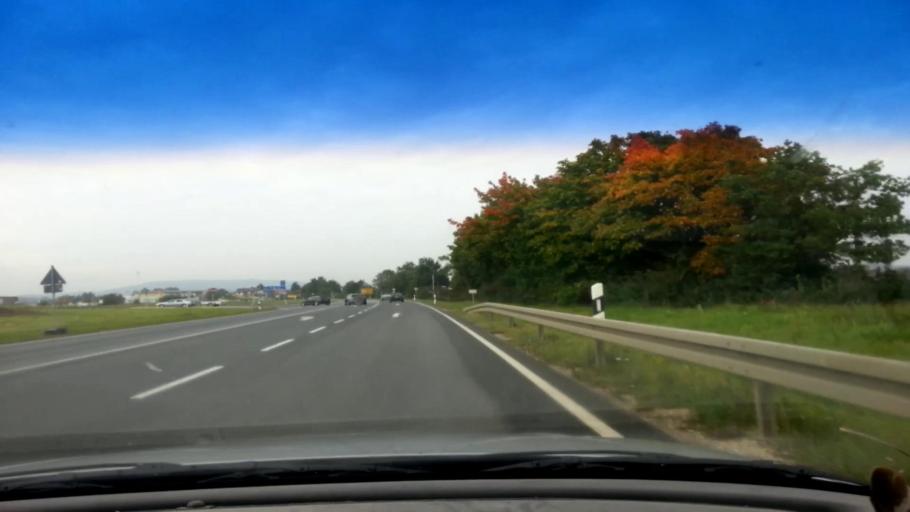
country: DE
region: Bavaria
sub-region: Upper Franconia
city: Kemmern
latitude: 49.9600
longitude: 10.8860
